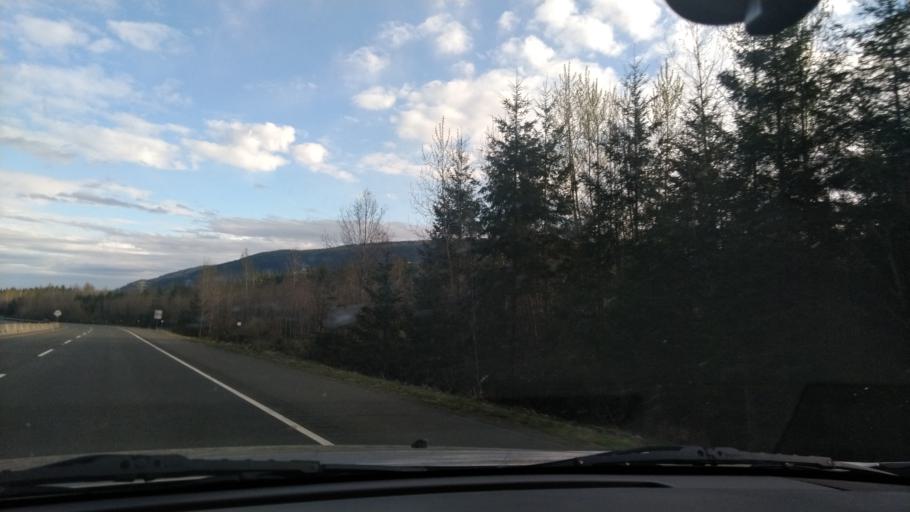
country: CA
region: British Columbia
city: Courtenay
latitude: 49.7847
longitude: -125.1420
